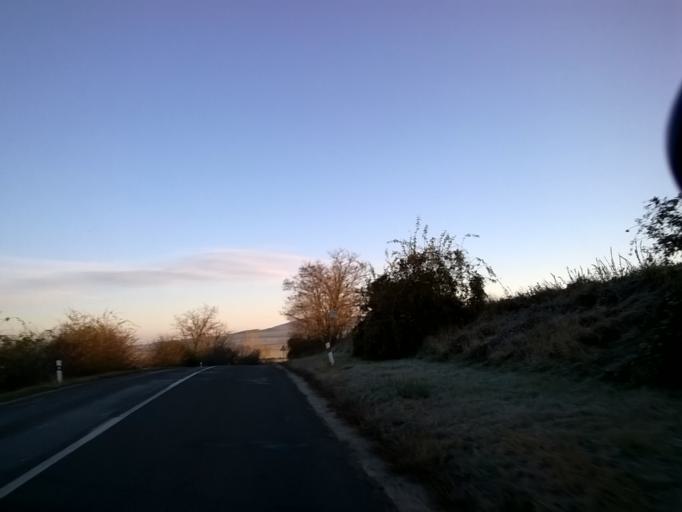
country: SK
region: Nitriansky
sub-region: Okres Nitra
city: Nitra
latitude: 48.3893
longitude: 18.0993
